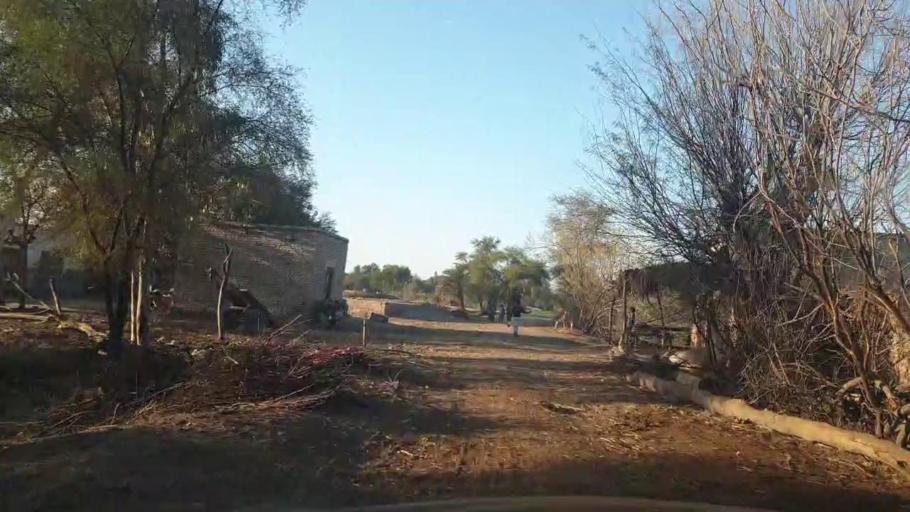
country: PK
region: Sindh
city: Mirpur Mathelo
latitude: 28.0049
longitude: 69.4652
